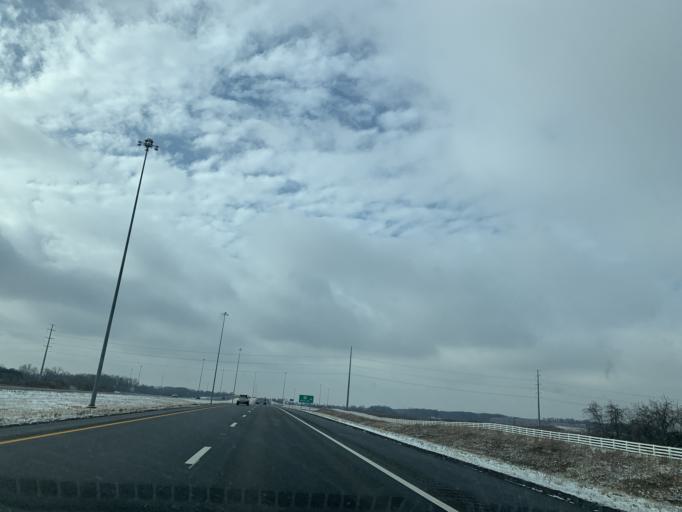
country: US
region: Ohio
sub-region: Franklin County
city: New Albany
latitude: 40.0809
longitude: -82.7444
